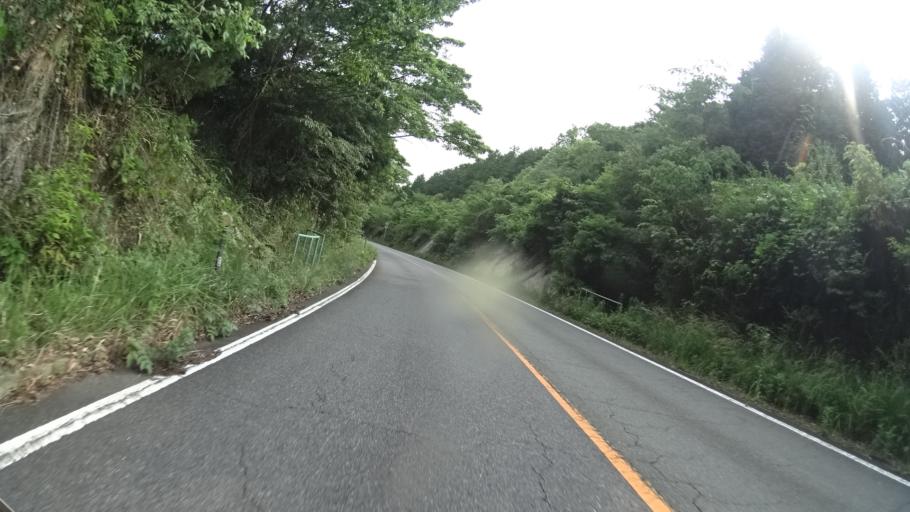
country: JP
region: Yamaguchi
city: Ogori-shimogo
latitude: 34.2332
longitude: 131.3063
